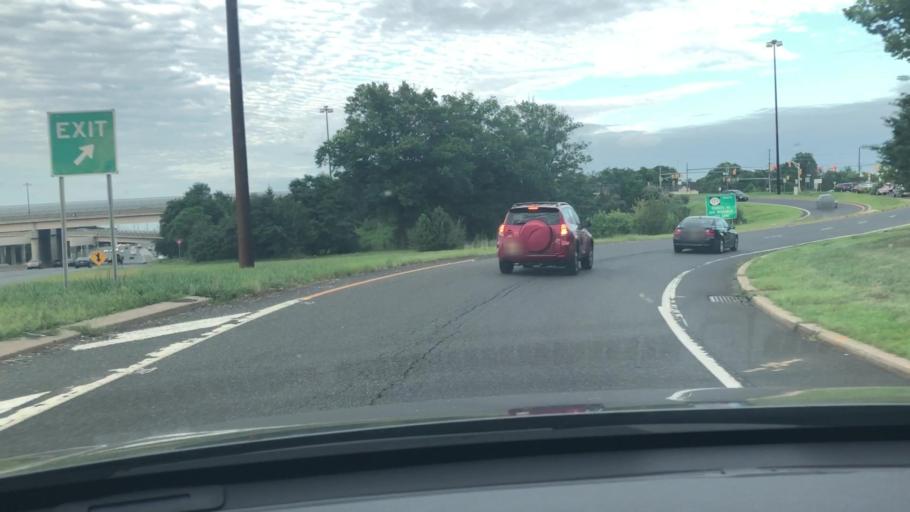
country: US
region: New Jersey
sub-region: Middlesex County
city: Milltown
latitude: 40.4620
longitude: -74.4574
